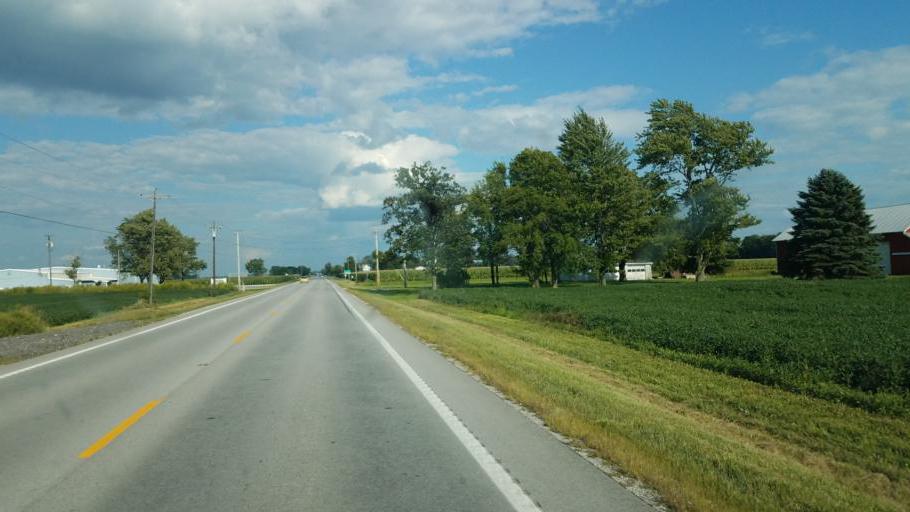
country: US
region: Ohio
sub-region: Wood County
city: Bowling Green
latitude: 41.3619
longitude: -83.5545
